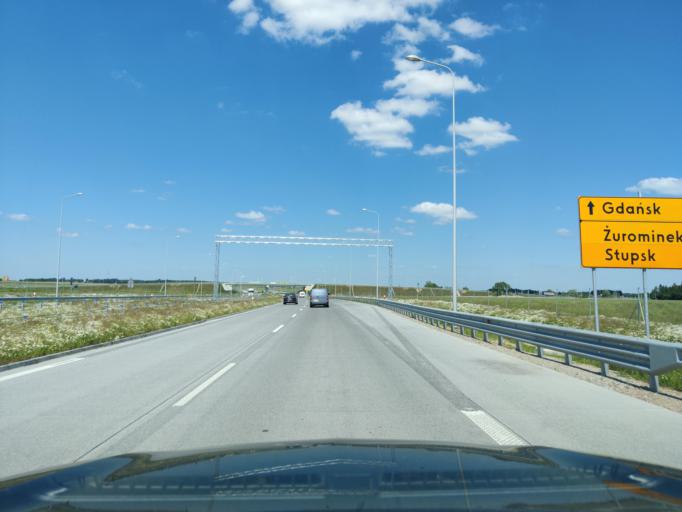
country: PL
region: Masovian Voivodeship
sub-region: Powiat mlawski
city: Wisniewo
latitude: 52.9863
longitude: 20.3438
